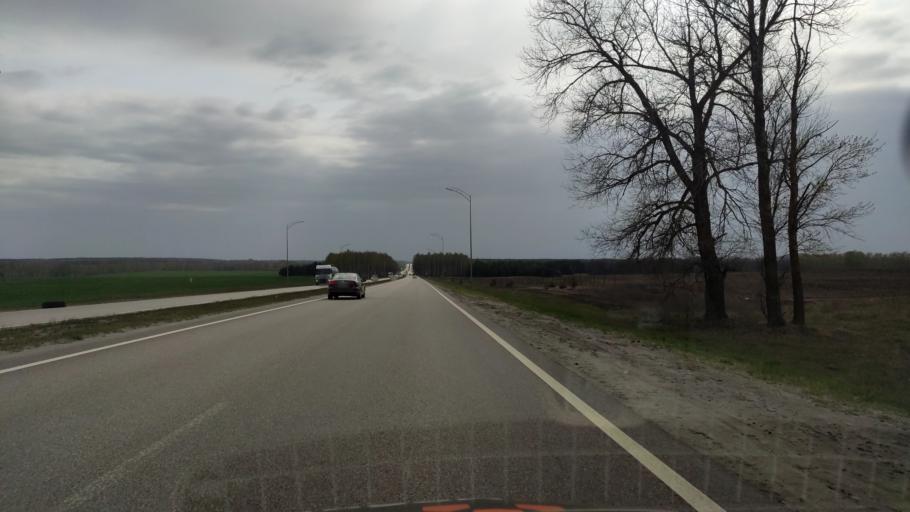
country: RU
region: Belgorod
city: Staryy Oskol
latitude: 51.4165
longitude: 37.8879
